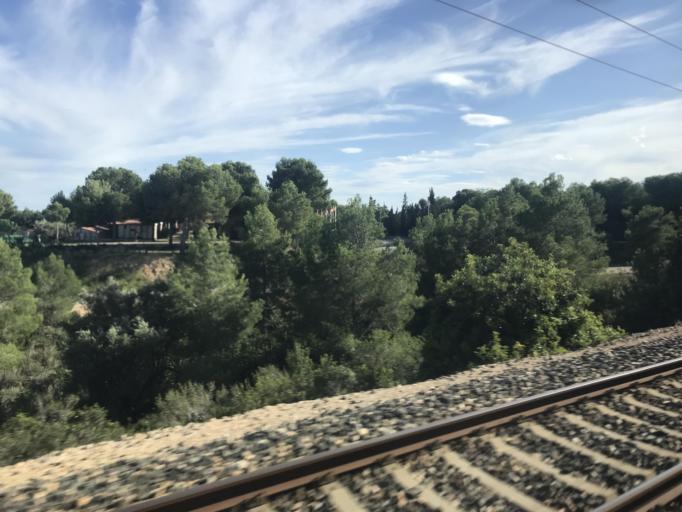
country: ES
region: Catalonia
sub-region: Provincia de Tarragona
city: l'Ametlla de Mar
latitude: 40.8665
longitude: 0.7786
